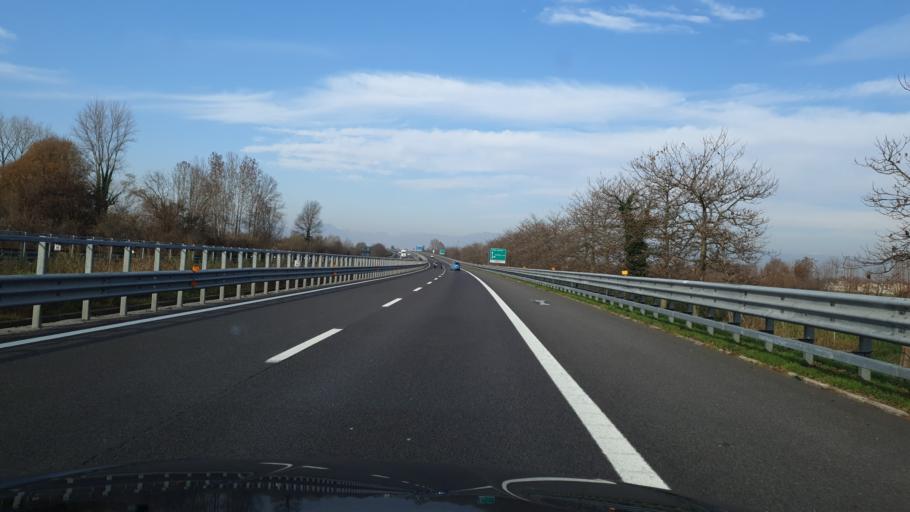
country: IT
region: Veneto
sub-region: Provincia di Vicenza
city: Lisiera
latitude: 45.5685
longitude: 11.6115
